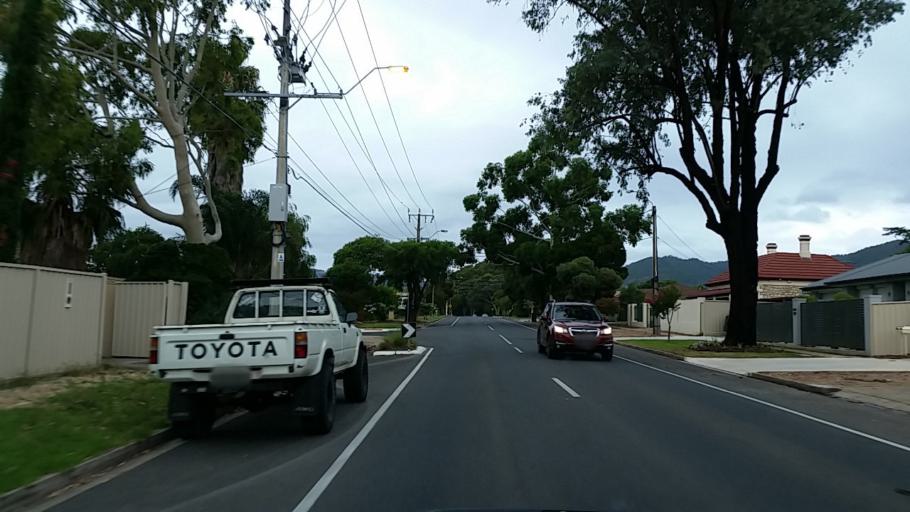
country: AU
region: South Australia
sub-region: Campbelltown
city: Athelstone
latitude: -34.8688
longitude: 138.6873
